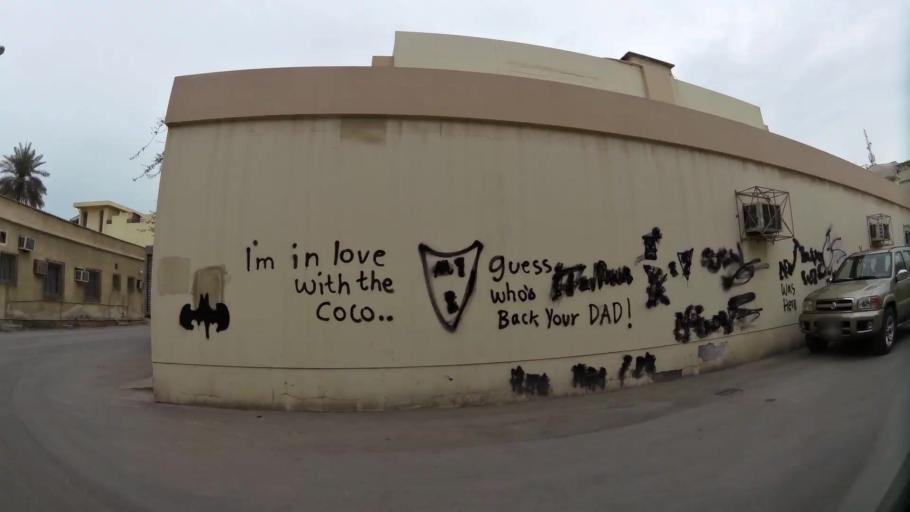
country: BH
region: Manama
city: Jidd Hafs
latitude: 26.2223
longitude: 50.5633
